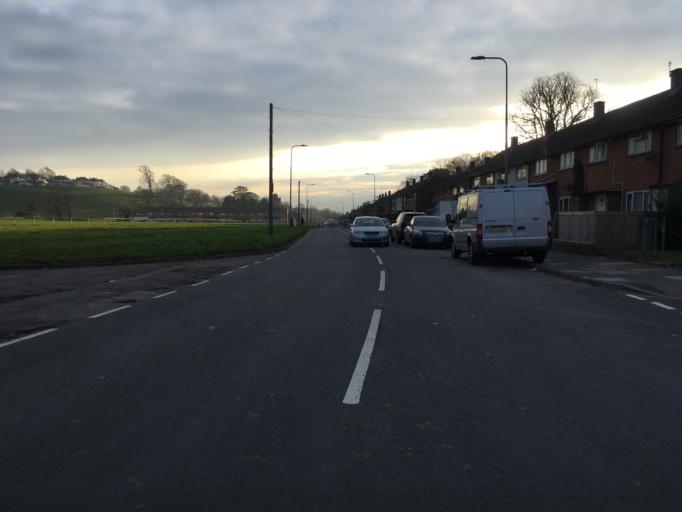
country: GB
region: Wales
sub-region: Newport
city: Marshfield
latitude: 51.5226
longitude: -3.1311
